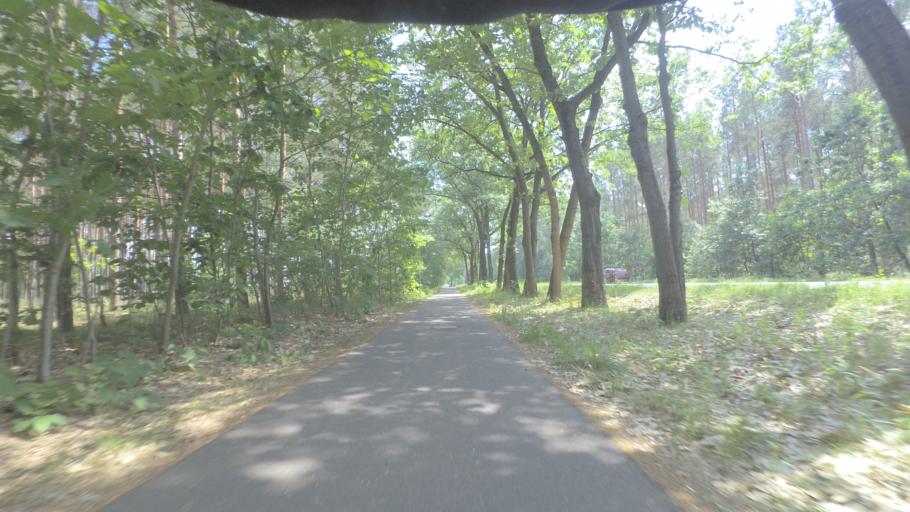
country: DE
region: Brandenburg
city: Beelitz
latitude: 52.2506
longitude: 12.9387
